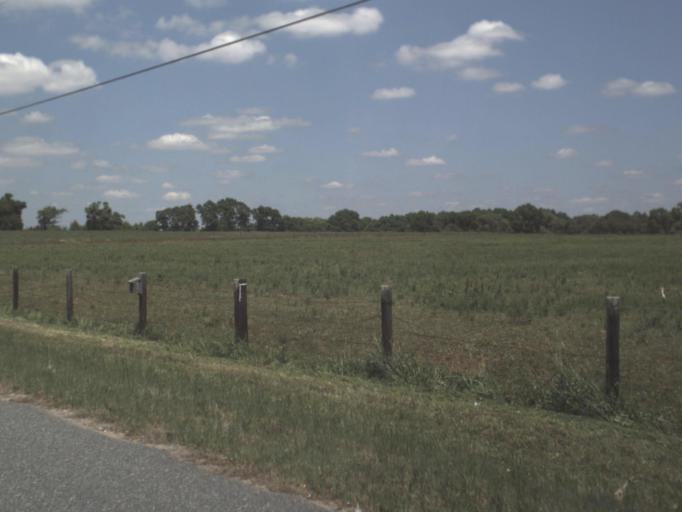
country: US
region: Florida
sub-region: Santa Rosa County
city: Point Baker
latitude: 30.8273
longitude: -87.0475
